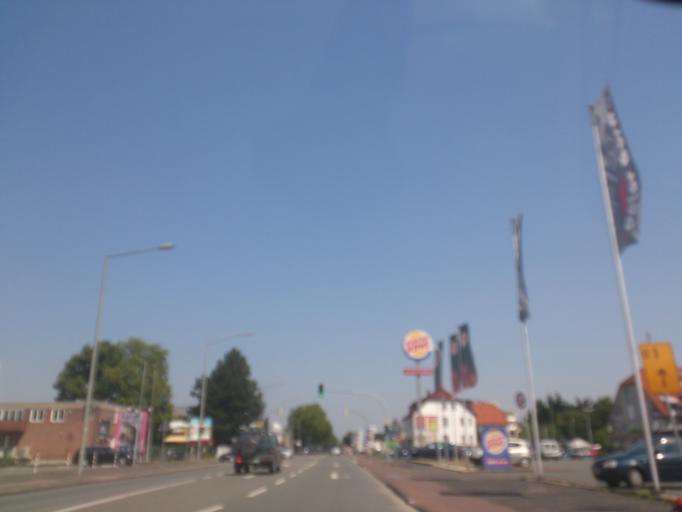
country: DE
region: North Rhine-Westphalia
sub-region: Regierungsbezirk Detmold
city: Paderborn
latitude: 51.7279
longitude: 8.7623
